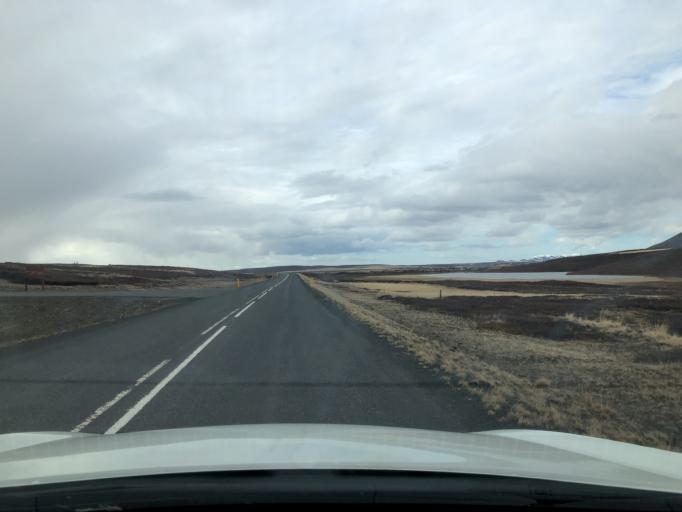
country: IS
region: Northeast
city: Laugar
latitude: 65.5731
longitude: -17.0861
